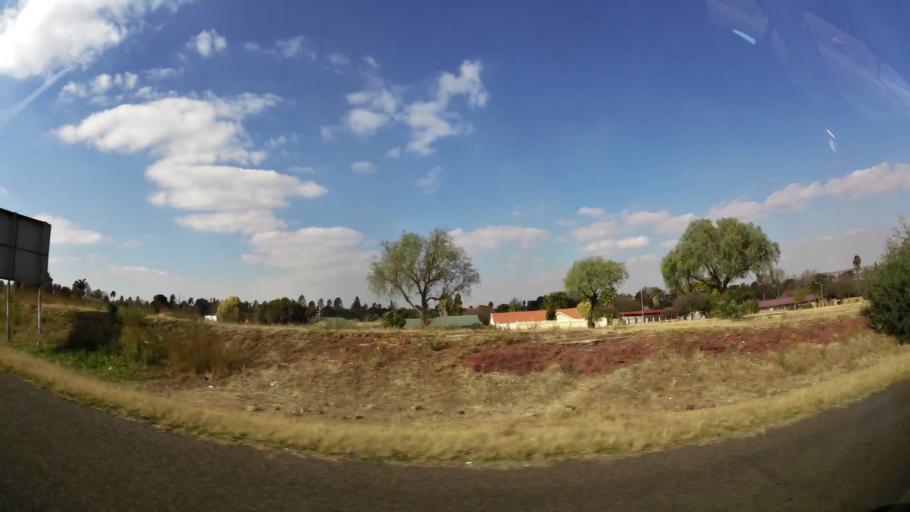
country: ZA
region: Gauteng
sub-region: West Rand District Municipality
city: Krugersdorp
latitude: -26.0794
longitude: 27.7602
